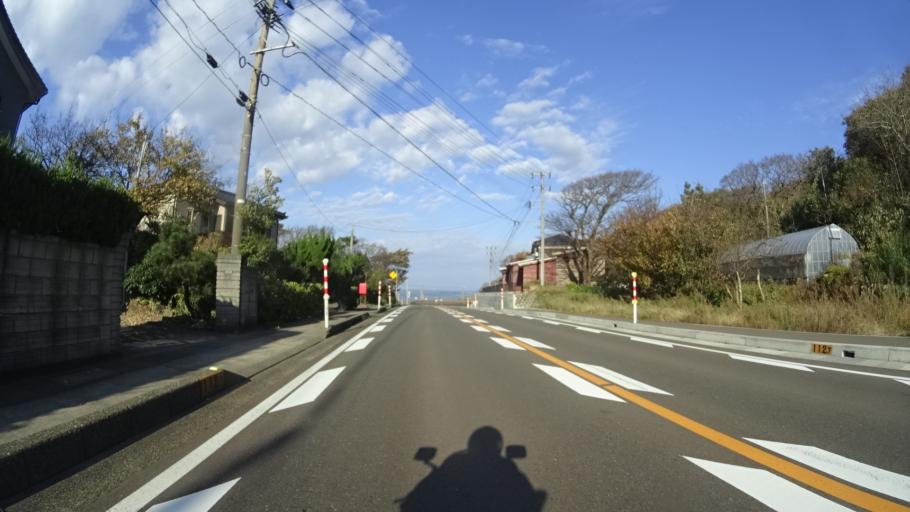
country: JP
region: Niigata
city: Kashiwazaki
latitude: 37.2962
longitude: 138.4070
